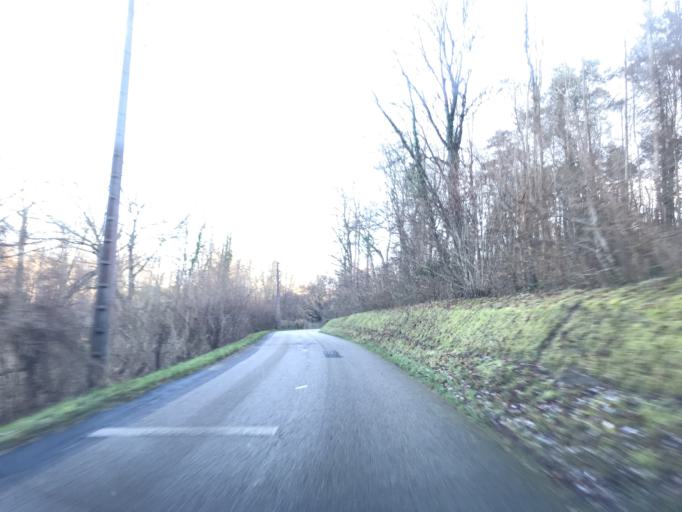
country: FR
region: Haute-Normandie
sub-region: Departement de l'Eure
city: Heudreville-sur-Eure
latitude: 49.0914
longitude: 1.2608
